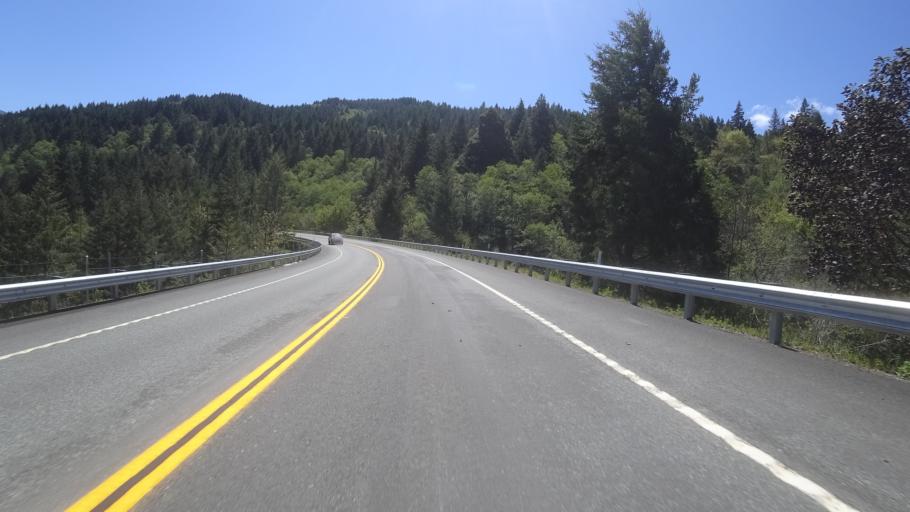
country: US
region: California
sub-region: Humboldt County
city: Blue Lake
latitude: 40.9061
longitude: -123.8290
